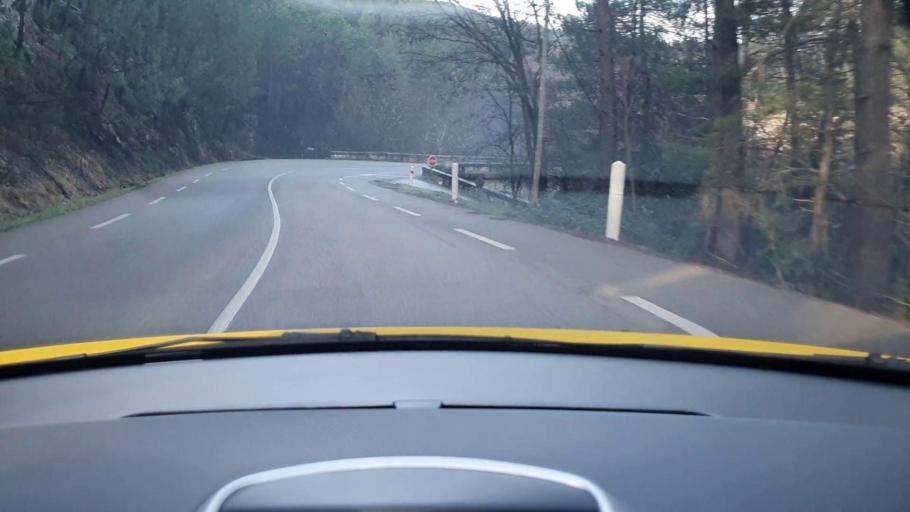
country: FR
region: Languedoc-Roussillon
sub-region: Departement du Gard
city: Les Salles-du-Gardon
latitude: 44.2503
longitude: 4.0477
